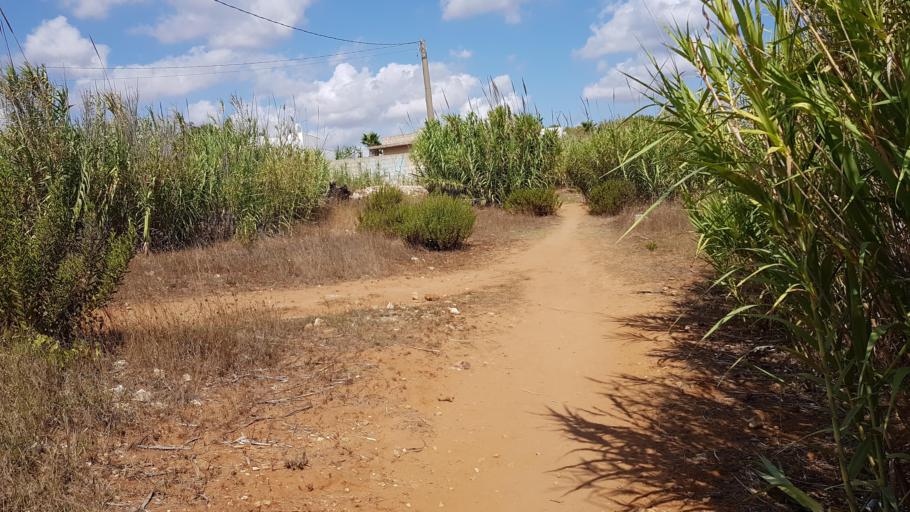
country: IT
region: Apulia
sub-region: Provincia di Brindisi
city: Torchiarolo
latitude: 40.5269
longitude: 18.0792
